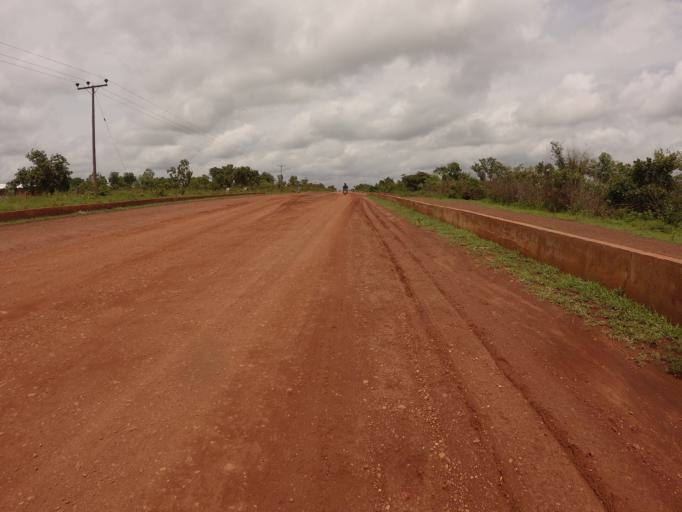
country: GH
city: Kpandae
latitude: 8.4523
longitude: 0.3474
